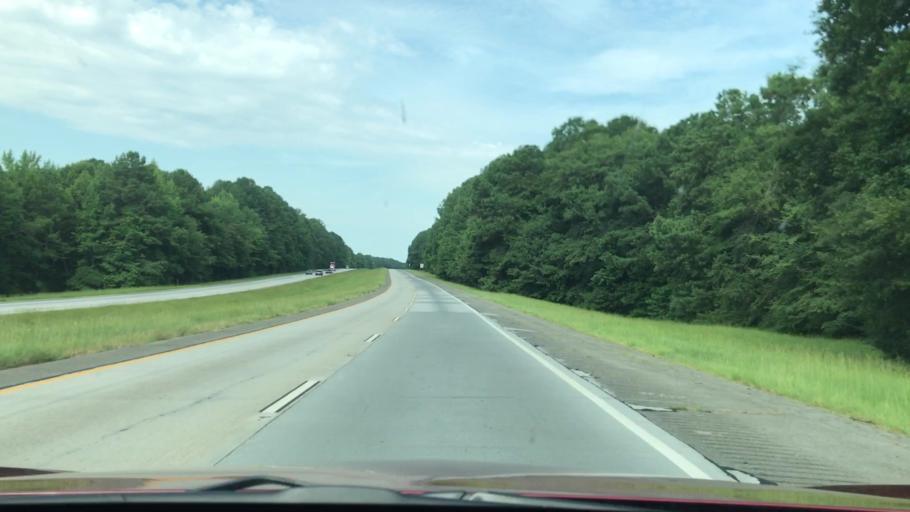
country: US
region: Georgia
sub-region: Warren County
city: Firing Range
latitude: 33.5034
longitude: -82.7703
